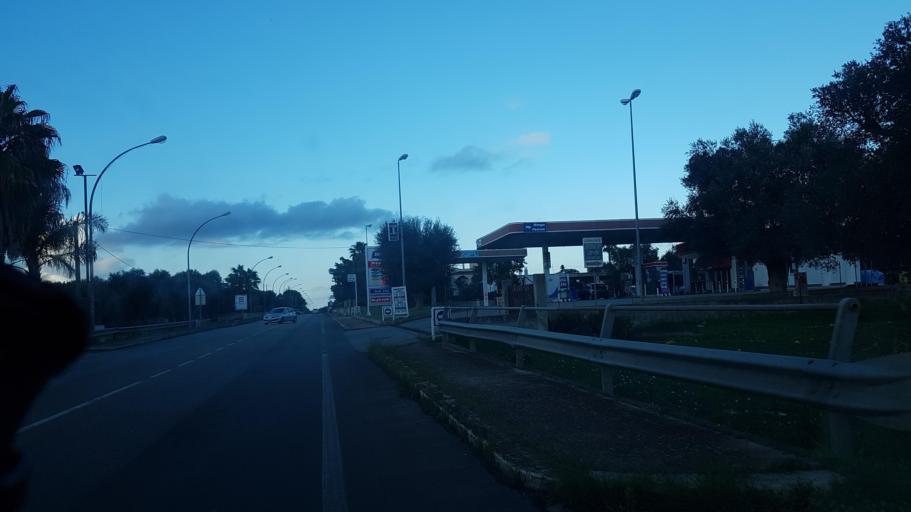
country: IT
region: Apulia
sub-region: Provincia di Brindisi
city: San Michele Salentino
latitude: 40.6388
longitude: 17.6321
